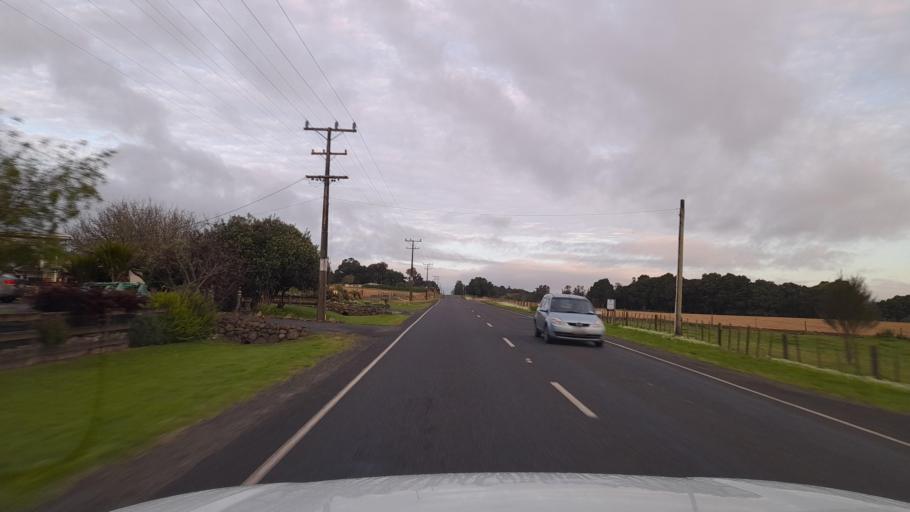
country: NZ
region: Northland
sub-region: Whangarei
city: Maungatapere
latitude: -35.7518
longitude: 174.1693
